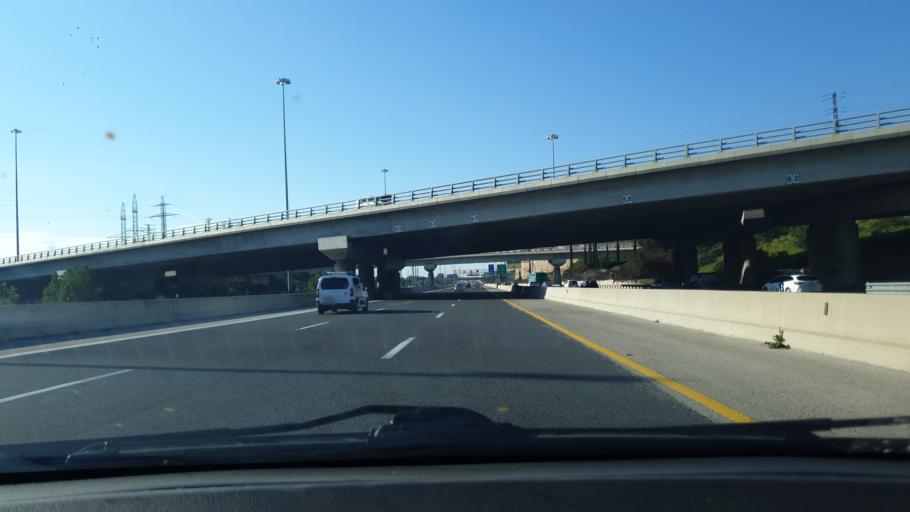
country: IL
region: Central District
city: Rishon LeZiyyon
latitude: 31.9578
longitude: 34.7758
